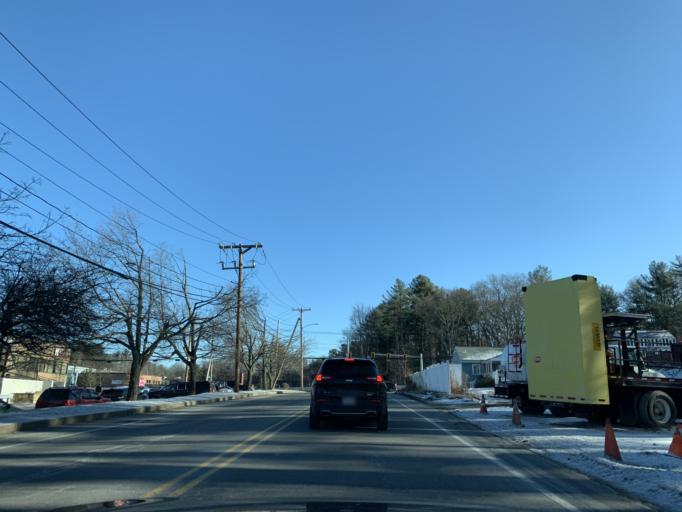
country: US
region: Massachusetts
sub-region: Norfolk County
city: Canton
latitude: 42.1904
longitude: -71.1510
